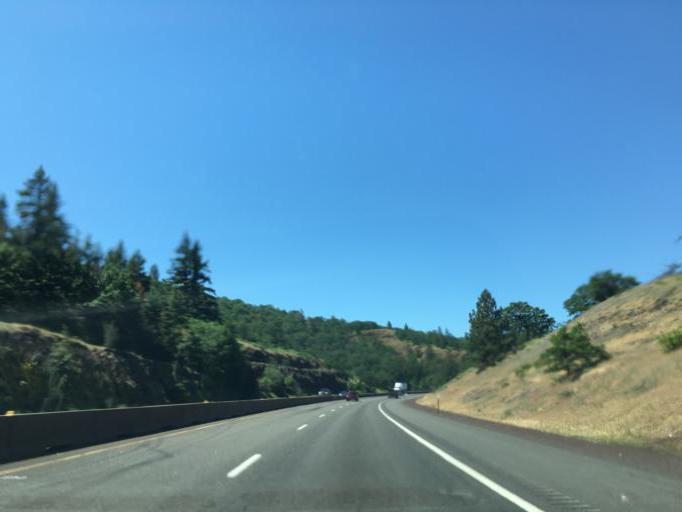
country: US
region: Oregon
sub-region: Wasco County
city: Chenoweth
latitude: 45.6935
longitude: -121.3239
